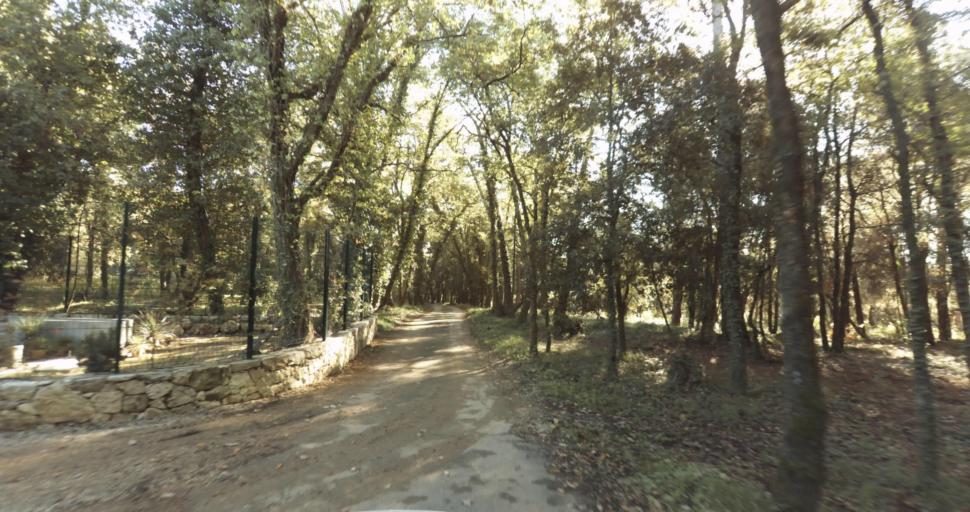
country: FR
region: Provence-Alpes-Cote d'Azur
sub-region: Departement des Alpes-Maritimes
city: Vence
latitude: 43.7102
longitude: 7.1031
